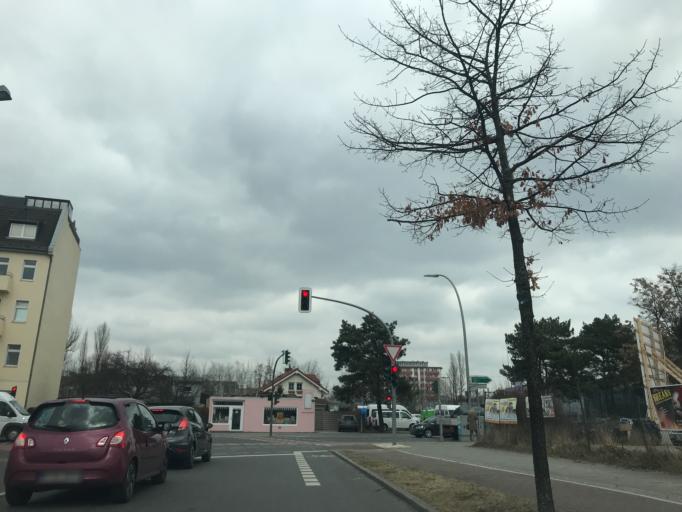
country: DE
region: Berlin
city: Wilhelmstadt
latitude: 52.5339
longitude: 13.1887
